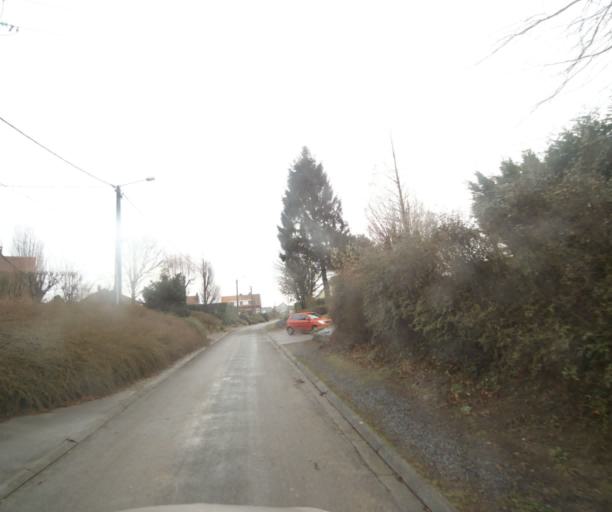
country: FR
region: Nord-Pas-de-Calais
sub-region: Departement du Nord
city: Famars
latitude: 50.2911
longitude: 3.5104
